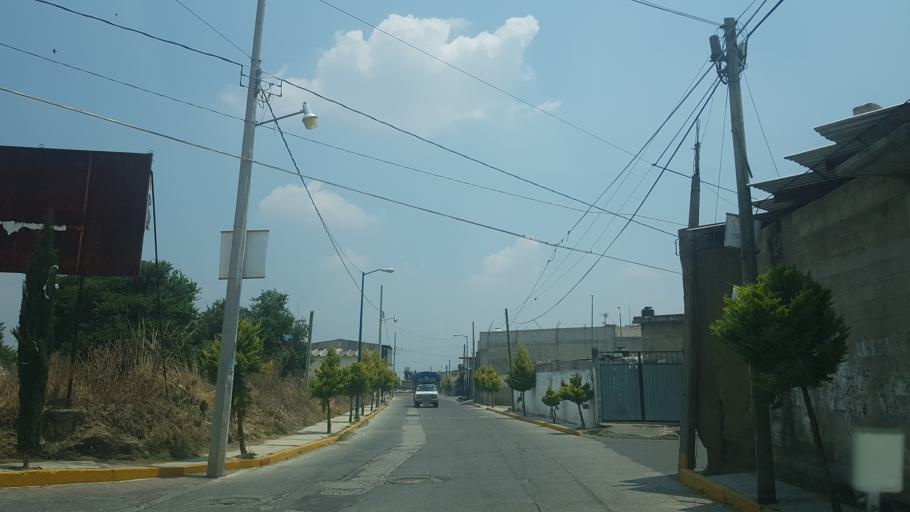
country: MX
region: Puebla
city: San Andres Calpan
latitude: 19.1033
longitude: -98.4529
